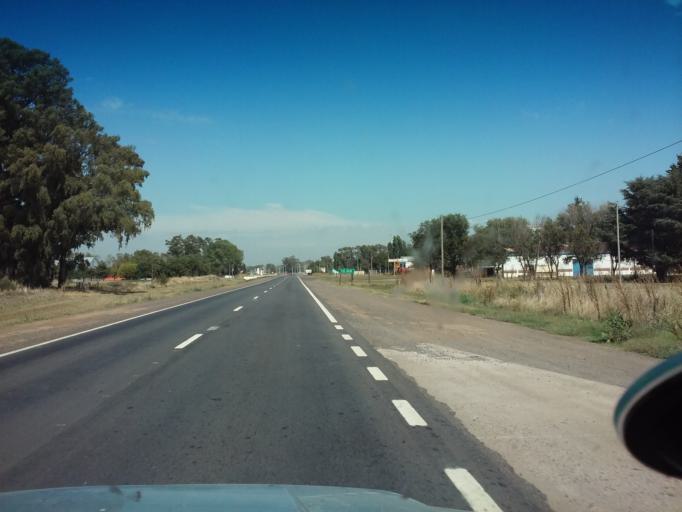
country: AR
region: Buenos Aires
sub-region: Partido de Nueve de Julio
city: Nueve de Julio
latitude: -35.4630
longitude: -60.8409
